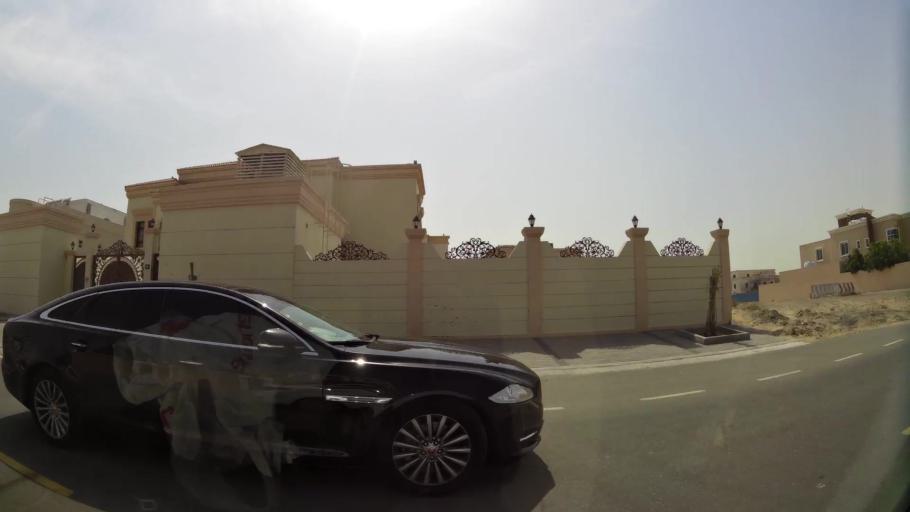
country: AE
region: Ash Shariqah
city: Sharjah
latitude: 25.2441
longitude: 55.4857
